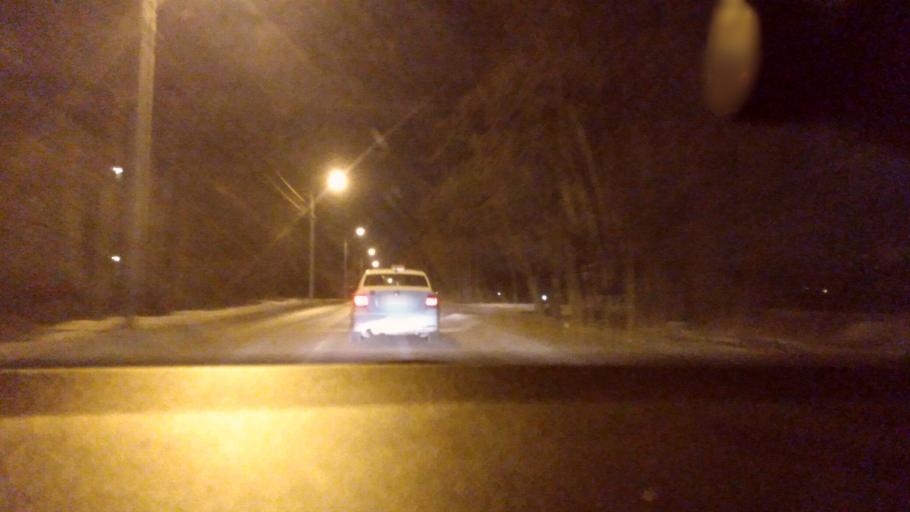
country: RU
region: Moskovskaya
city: Zheleznodorozhnyy
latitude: 55.7397
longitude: 38.0404
